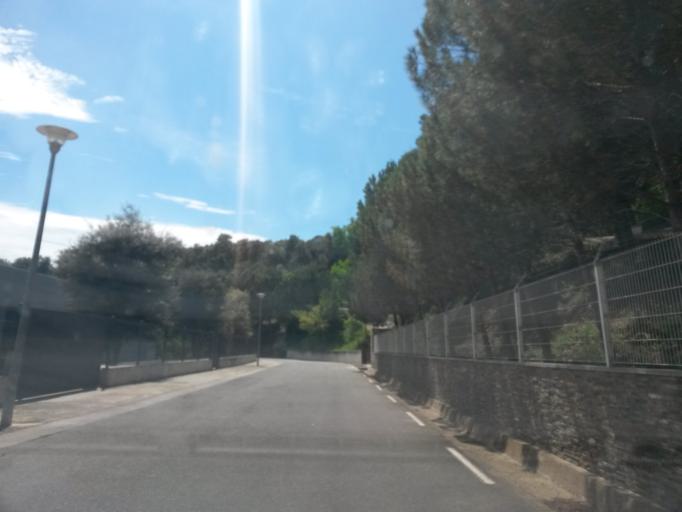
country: ES
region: Catalonia
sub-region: Provincia de Girona
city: Vilablareix
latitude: 41.9646
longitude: 2.7594
